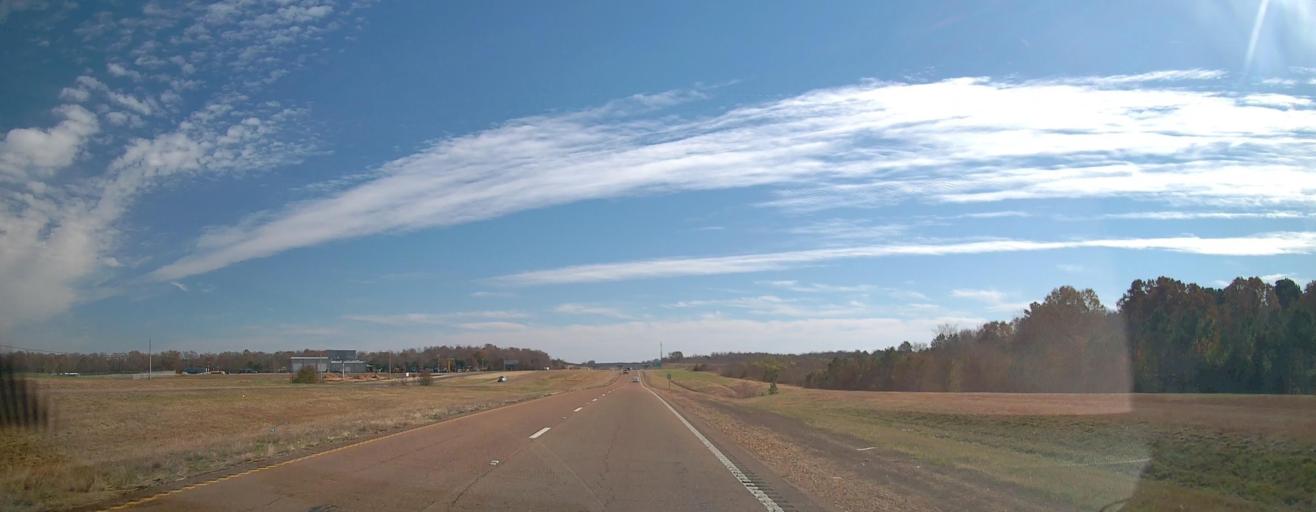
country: US
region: Tennessee
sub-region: Fayette County
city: Piperton
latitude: 34.9696
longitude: -89.5545
